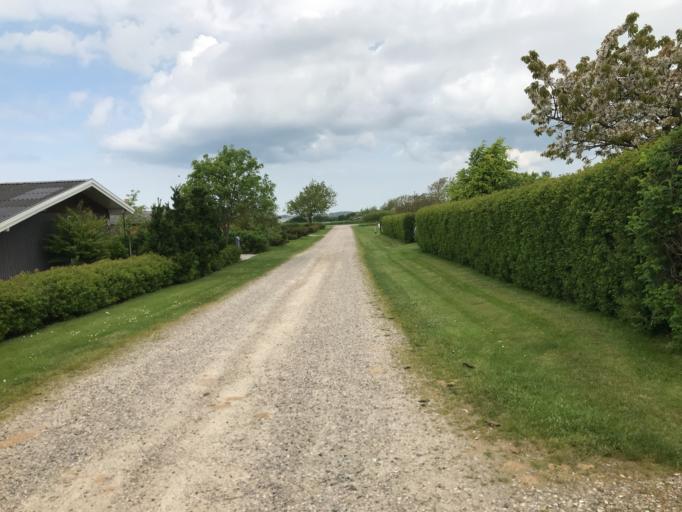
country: DK
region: South Denmark
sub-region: Assens Kommune
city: Assens
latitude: 55.3332
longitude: 9.8798
